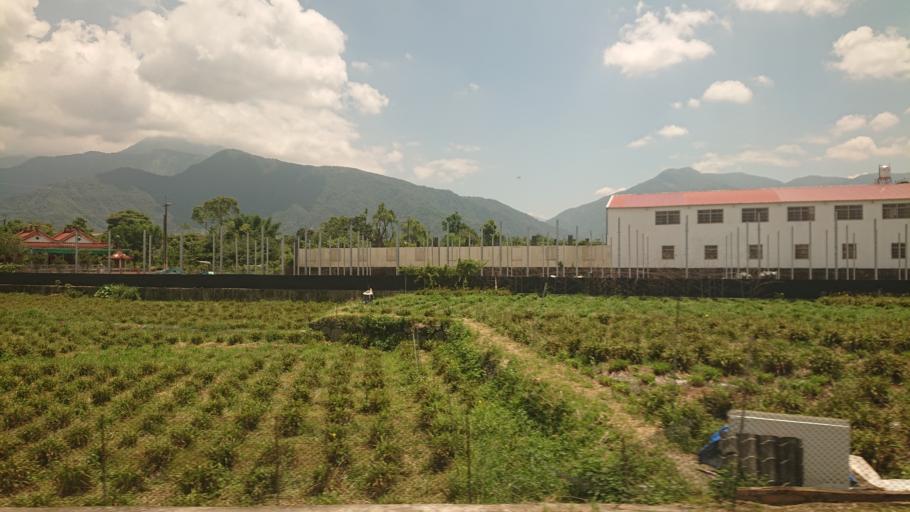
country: TW
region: Taiwan
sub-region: Nantou
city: Puli
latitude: 23.9790
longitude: 120.9611
